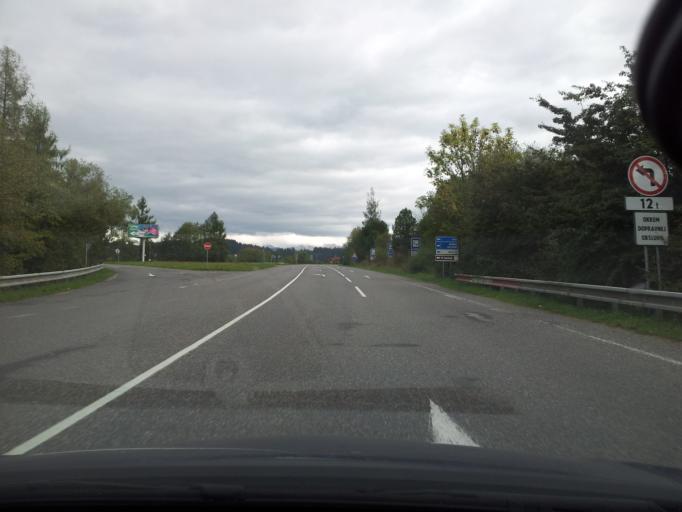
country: SK
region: Zilinsky
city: Ruzomberok
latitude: 49.0944
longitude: 19.4299
